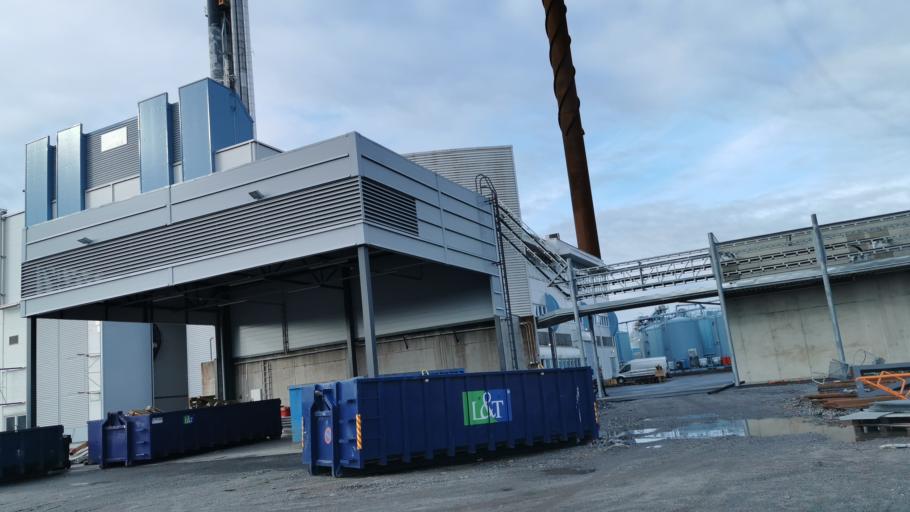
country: FI
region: Ostrobothnia
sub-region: Vaasa
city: Vaasa
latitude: 63.0906
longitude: 21.5587
